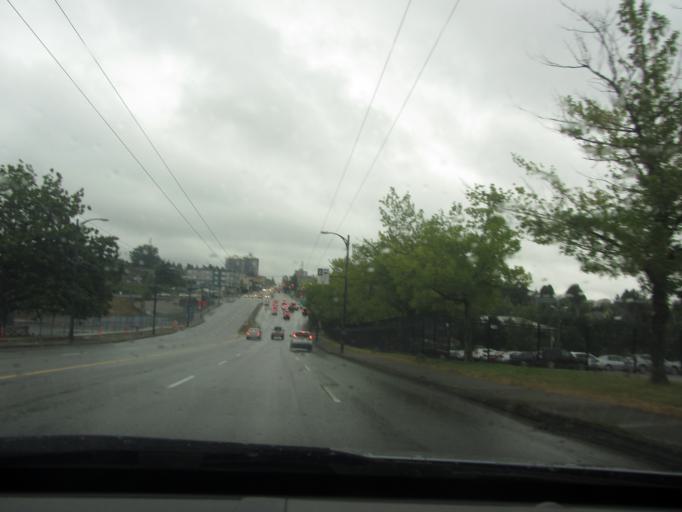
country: CA
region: British Columbia
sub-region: Fraser Valley Regional District
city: North Vancouver
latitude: 49.2811
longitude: -123.0349
